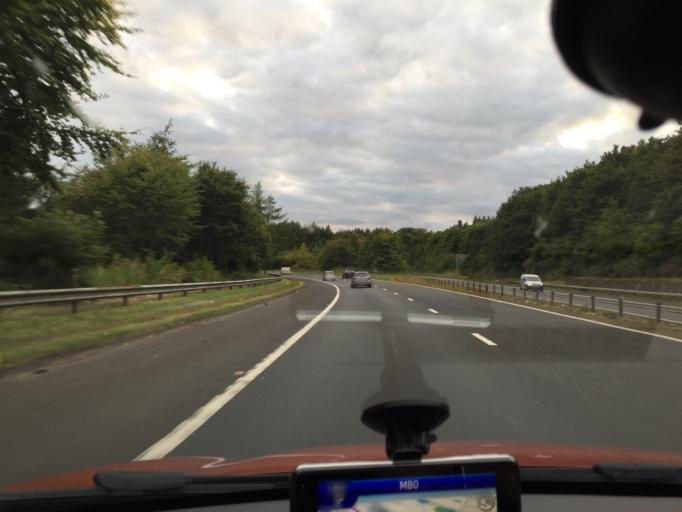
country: GB
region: Scotland
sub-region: Falkirk
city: Denny
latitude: 56.0023
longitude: -3.9115
